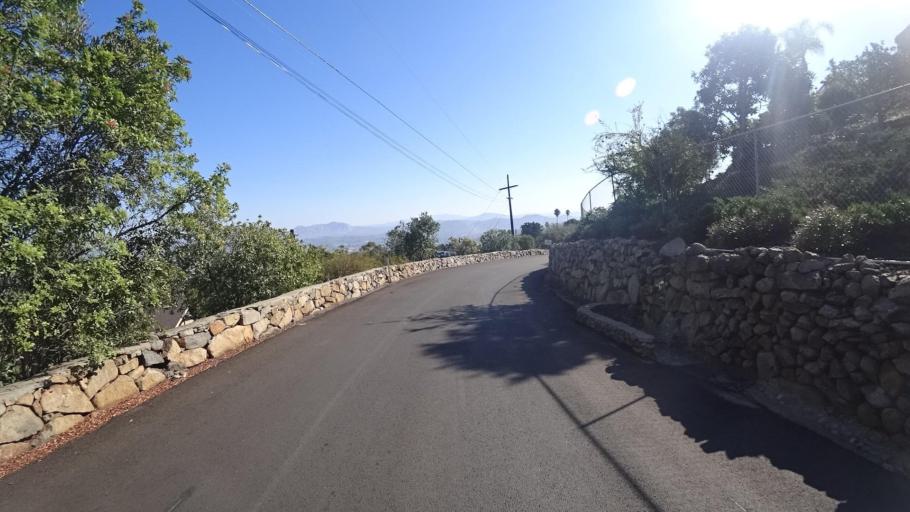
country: US
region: California
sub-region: San Diego County
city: Casa de Oro-Mount Helix
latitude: 32.7709
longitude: -116.9817
